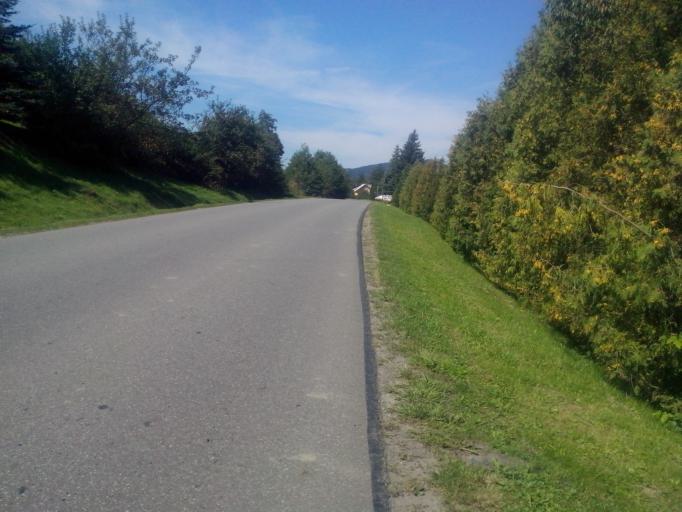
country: PL
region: Subcarpathian Voivodeship
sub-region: Powiat strzyzowski
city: Frysztak
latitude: 49.8668
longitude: 21.6098
